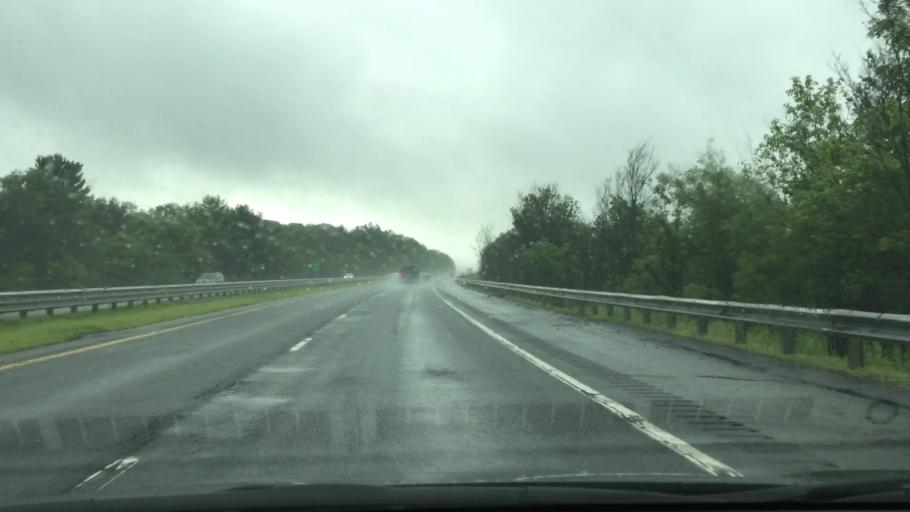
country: US
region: Massachusetts
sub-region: Worcester County
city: Warren
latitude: 42.1667
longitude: -72.1802
